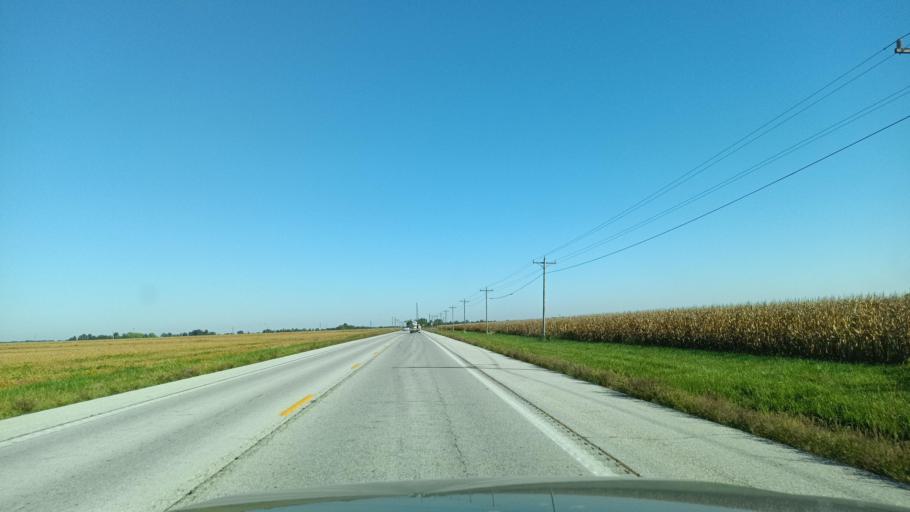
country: US
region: Missouri
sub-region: Audrain County
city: Vandalia
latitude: 39.4353
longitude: -91.6363
